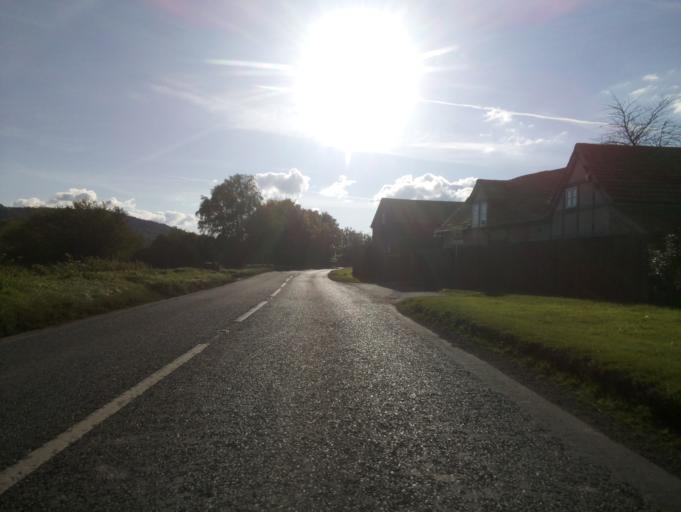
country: GB
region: England
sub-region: Herefordshire
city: Dorstone
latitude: 52.1209
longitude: -3.0040
